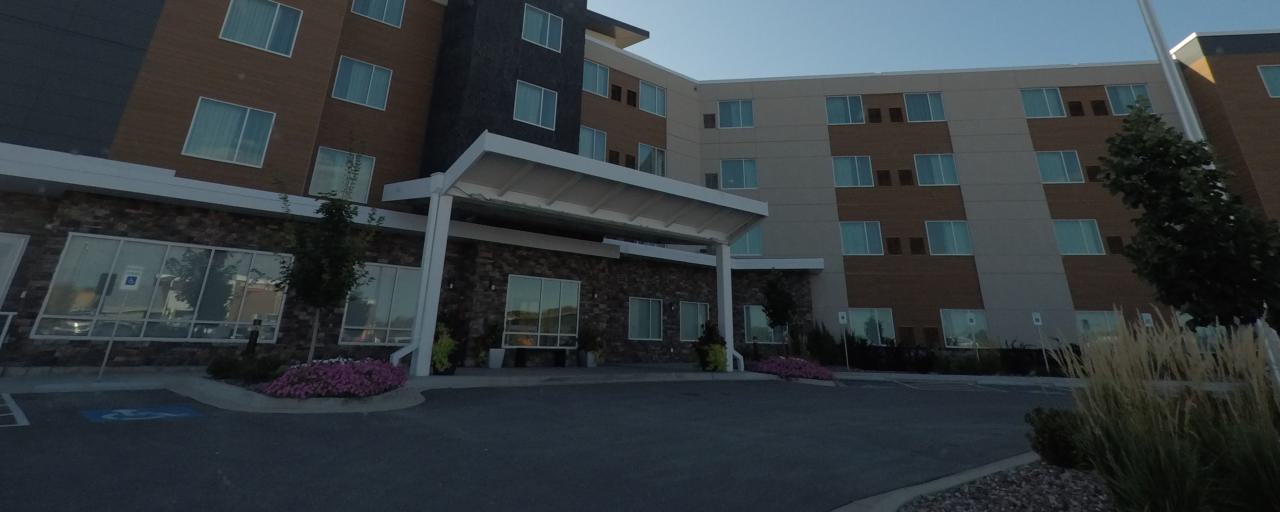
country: US
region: Missouri
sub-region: Clay County
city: Liberty
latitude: 39.2436
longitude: -94.4546
